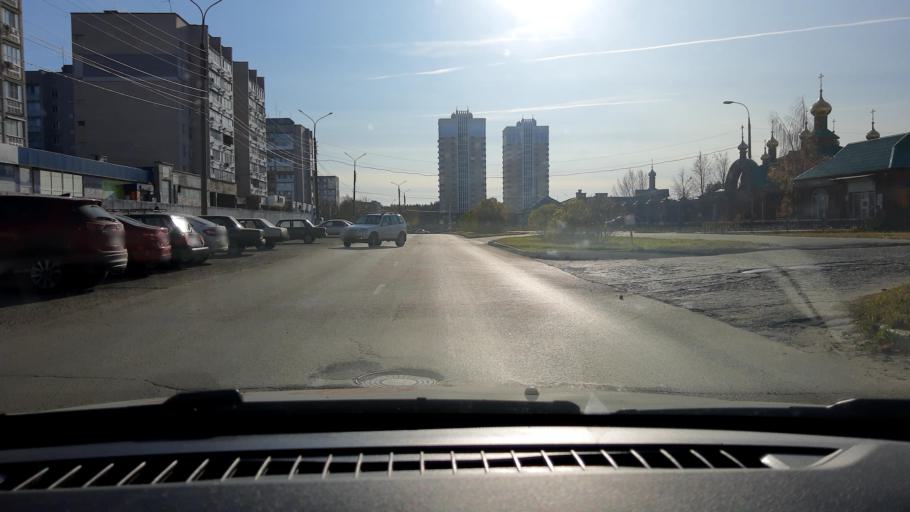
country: RU
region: Nizjnij Novgorod
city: Dzerzhinsk
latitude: 56.2307
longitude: 43.4164
